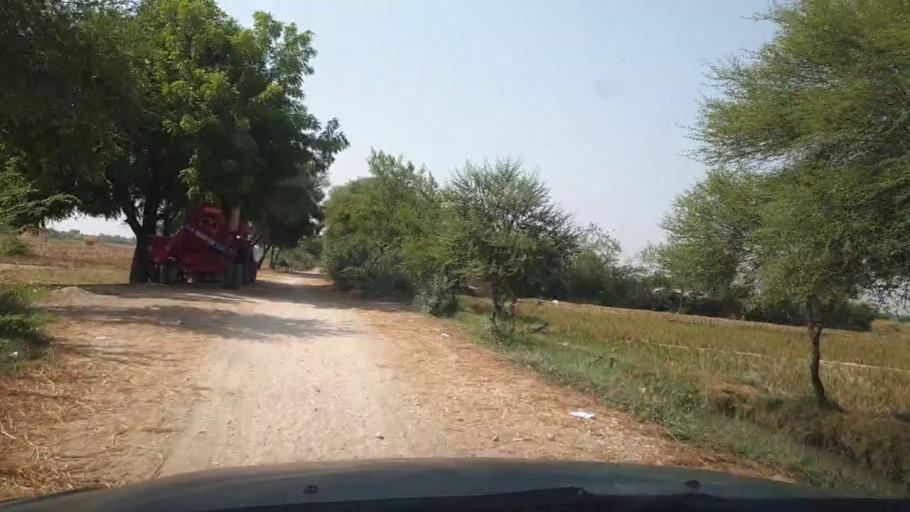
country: PK
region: Sindh
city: Bulri
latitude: 24.8722
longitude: 68.3182
